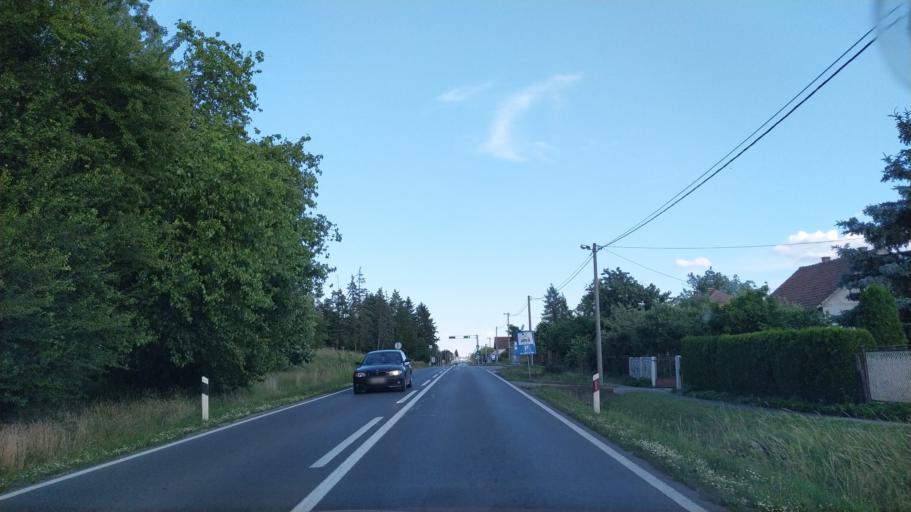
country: HR
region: Virovitick-Podravska
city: Spisic-Bukovica
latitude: 45.8524
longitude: 17.3287
